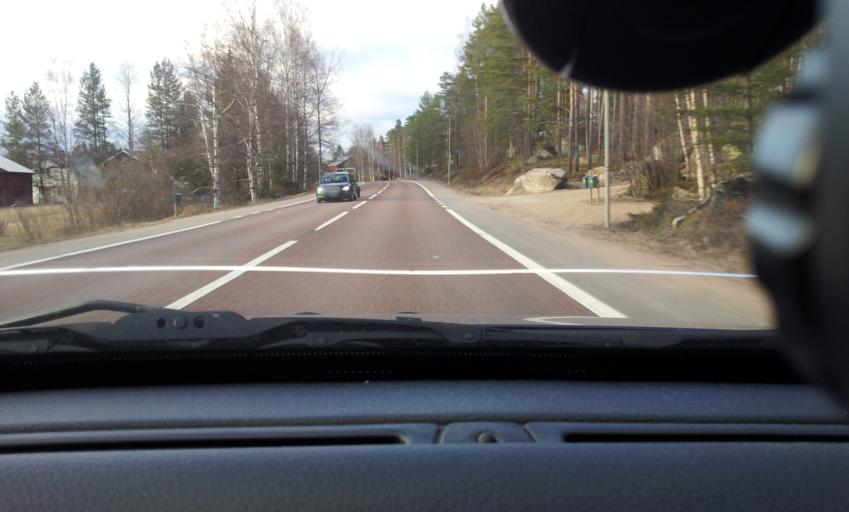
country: SE
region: Jaemtland
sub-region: Harjedalens Kommun
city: Sveg
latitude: 62.1637
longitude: 14.9497
